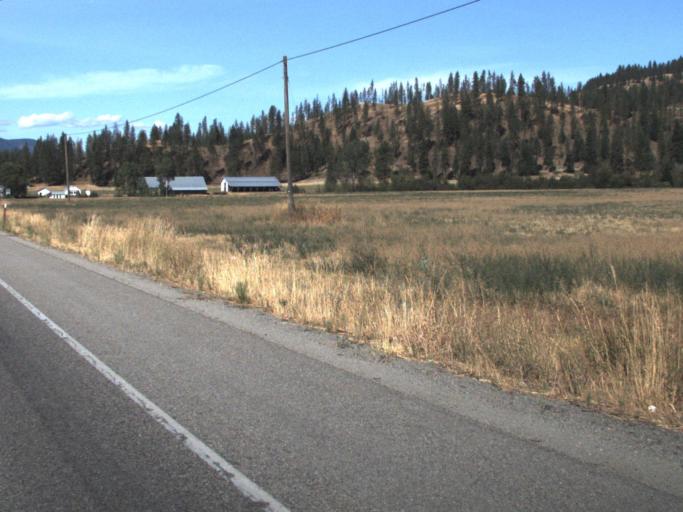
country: US
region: Washington
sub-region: Stevens County
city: Chewelah
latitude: 48.3151
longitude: -117.8080
